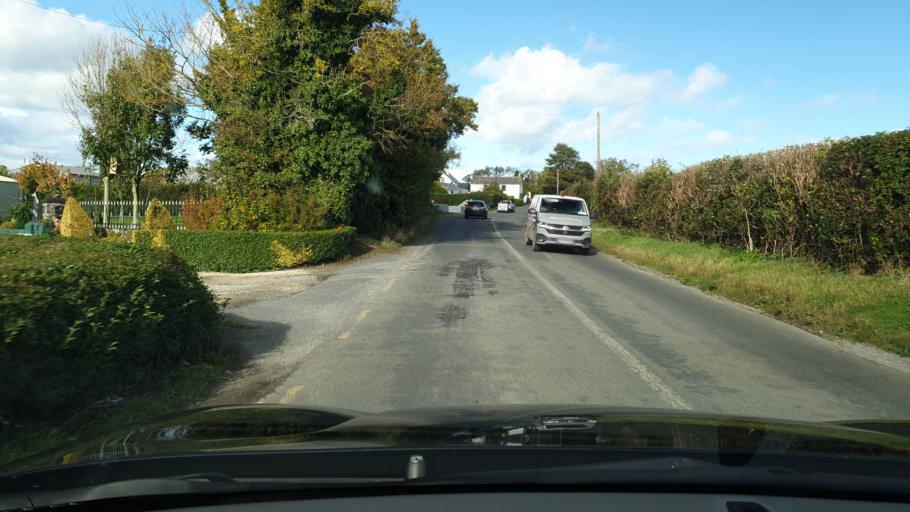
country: IE
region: Leinster
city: An Ros
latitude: 53.5511
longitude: -6.1021
